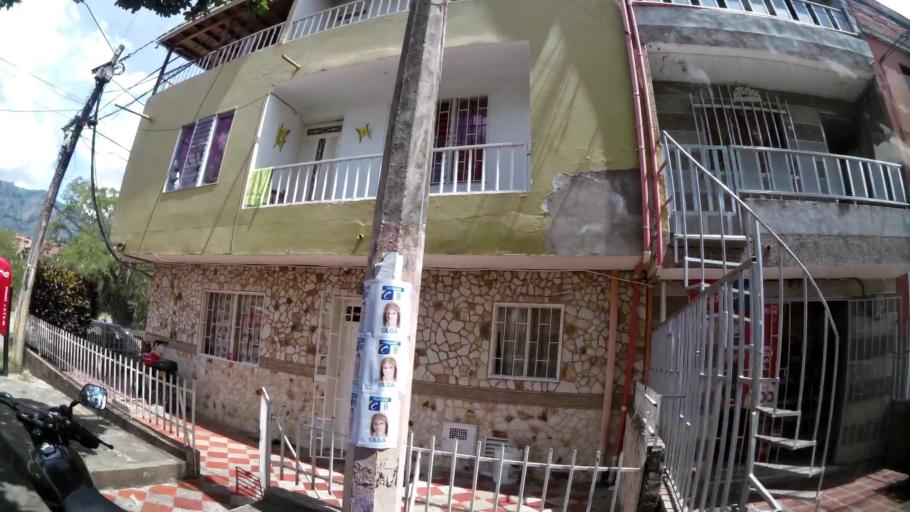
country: CO
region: Antioquia
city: Bello
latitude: 6.3467
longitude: -75.5570
